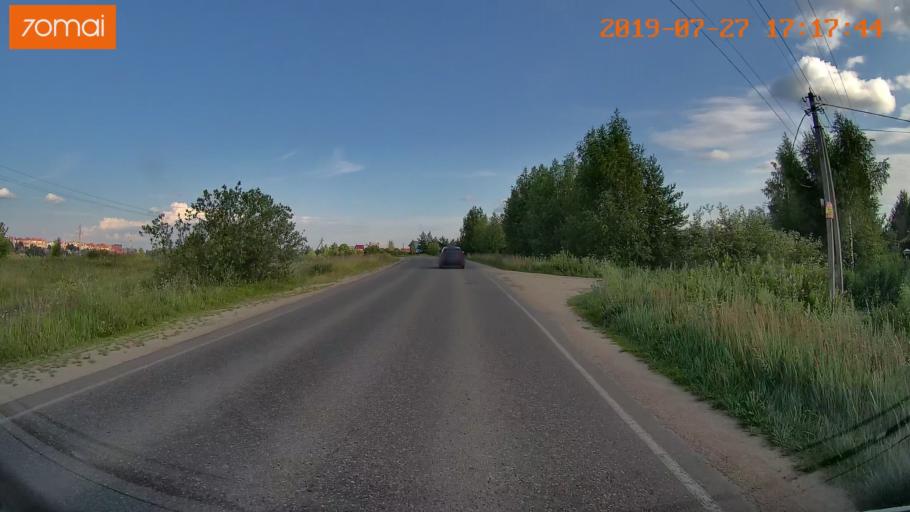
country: RU
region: Ivanovo
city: Novo-Talitsy
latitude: 57.0348
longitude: 40.8978
